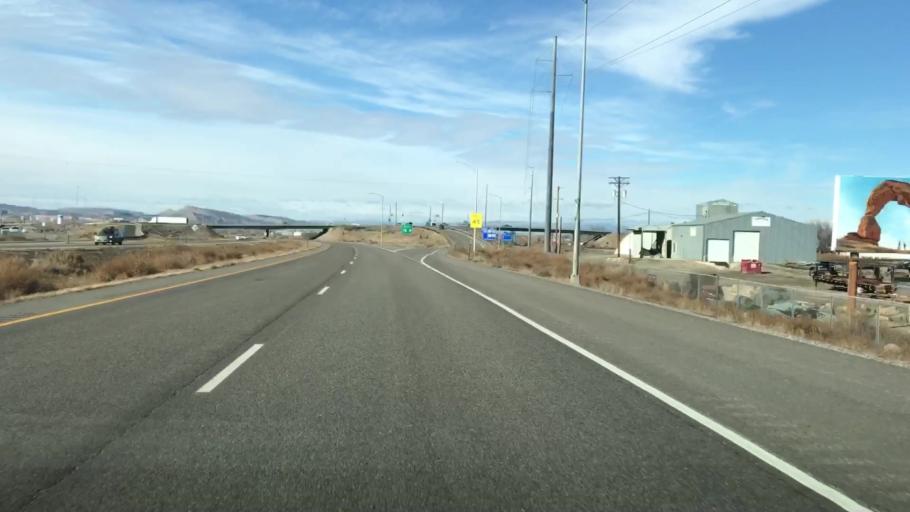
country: US
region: Colorado
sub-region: Mesa County
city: Fruita
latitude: 39.1519
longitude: -108.7323
